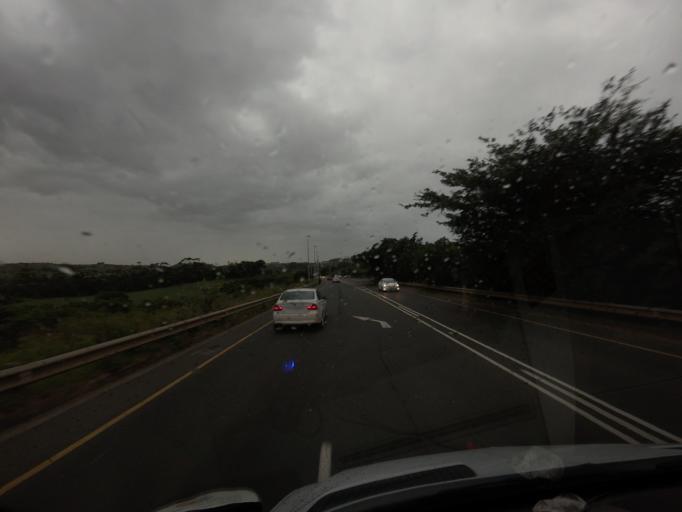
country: ZA
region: KwaZulu-Natal
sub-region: iLembe District Municipality
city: Ballitoville
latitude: -29.5443
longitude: 31.1917
